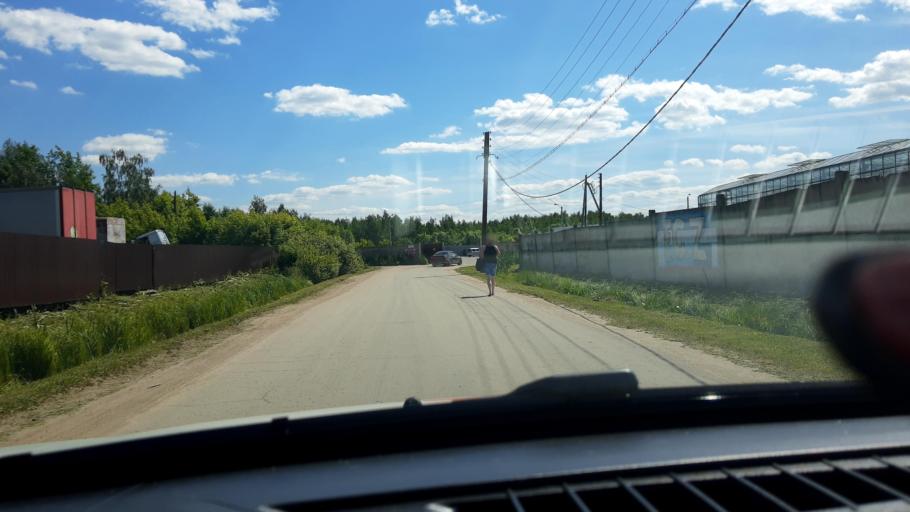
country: RU
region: Nizjnij Novgorod
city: Gorbatovka
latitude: 56.3054
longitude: 43.8142
